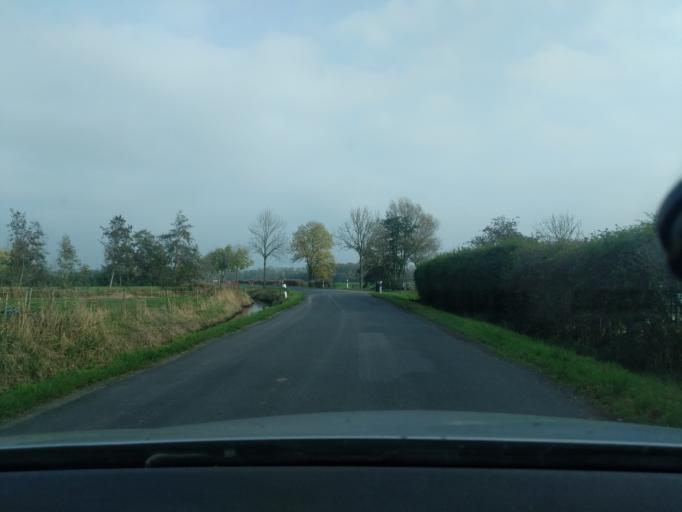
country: DE
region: Lower Saxony
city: Ihlienworth
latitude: 53.7342
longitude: 8.8996
